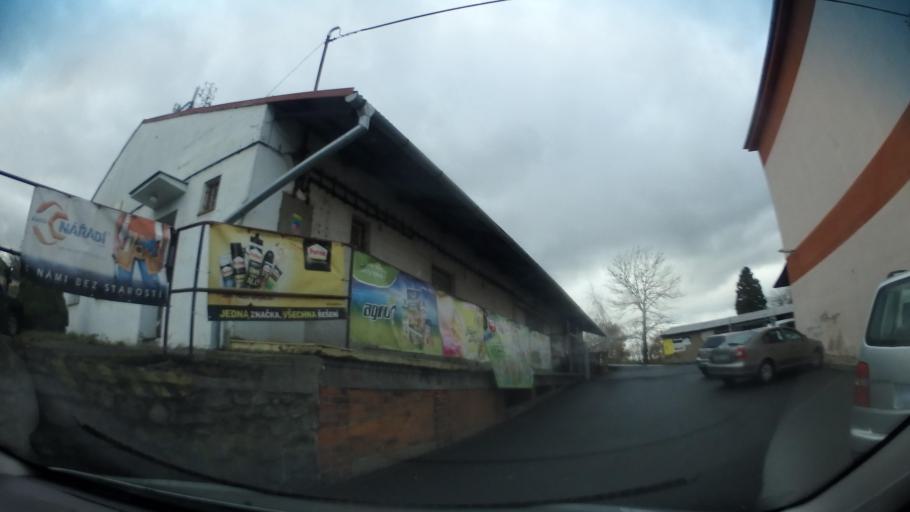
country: CZ
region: Vysocina
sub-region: Okres Zd'ar nad Sazavou
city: Velka Bites
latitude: 49.2835
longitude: 16.2263
